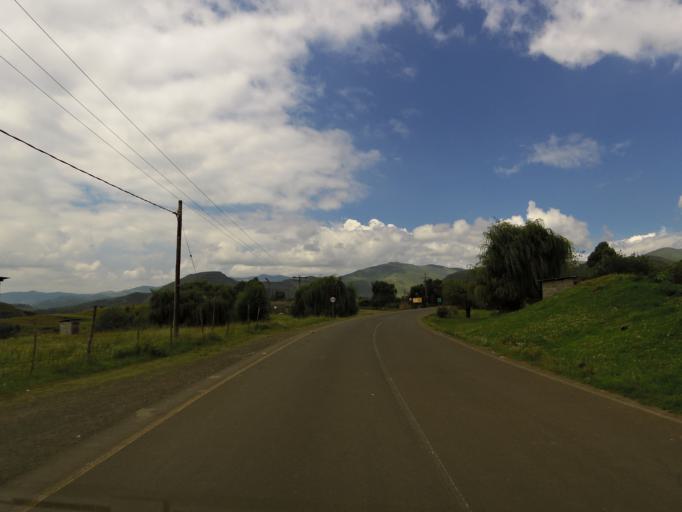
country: LS
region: Butha-Buthe
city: Butha-Buthe
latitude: -29.1079
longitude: 28.4876
